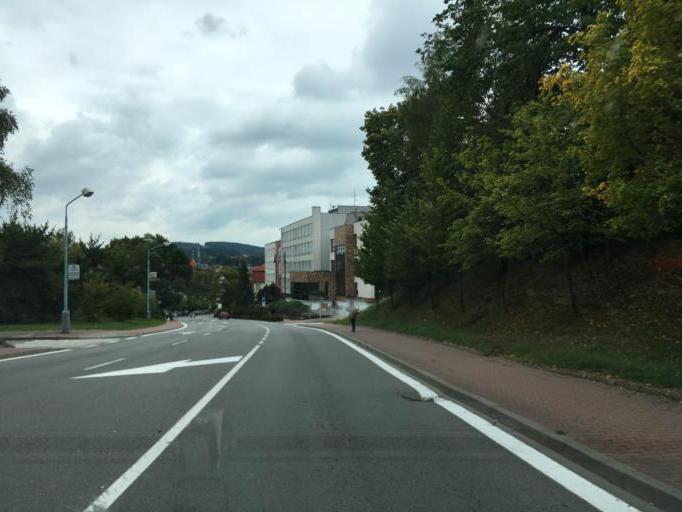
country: CZ
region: Vysocina
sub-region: Okres Pelhrimov
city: Pelhrimov
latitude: 49.4347
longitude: 15.2196
